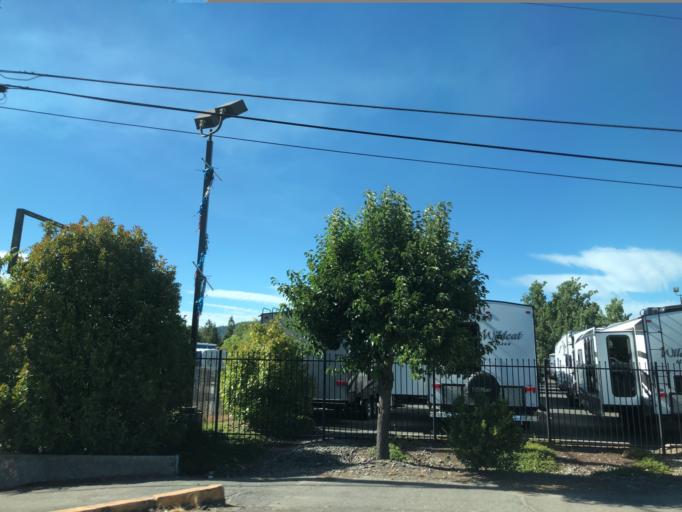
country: US
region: Oregon
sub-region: Josephine County
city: Grants Pass
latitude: 42.4244
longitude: -123.3360
